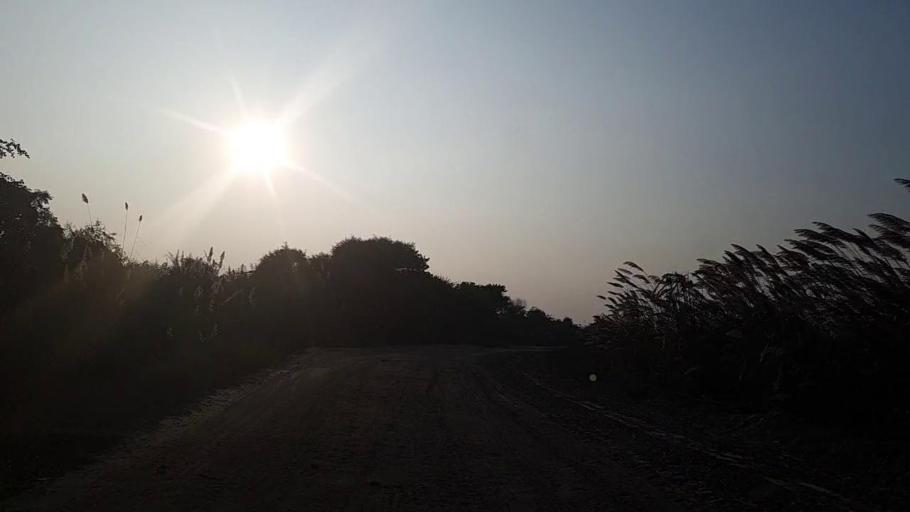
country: PK
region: Sindh
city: Mirpur Sakro
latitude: 24.5580
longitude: 67.5991
